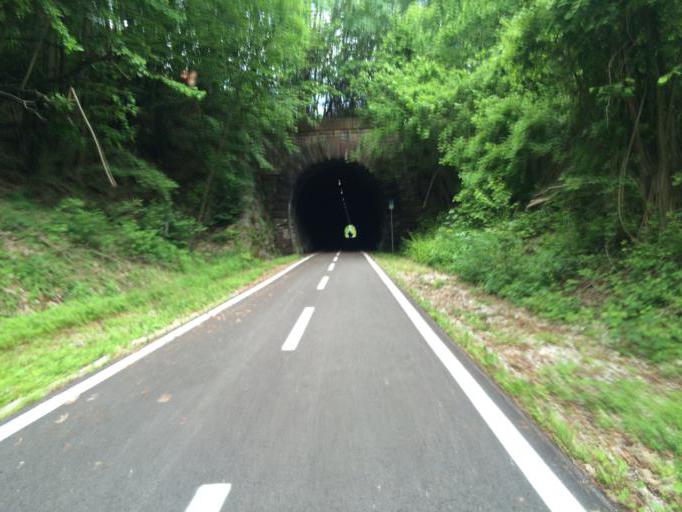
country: IT
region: Friuli Venezia Giulia
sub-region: Provincia di Udine
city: Malborghetto
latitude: 46.5023
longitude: 13.4329
